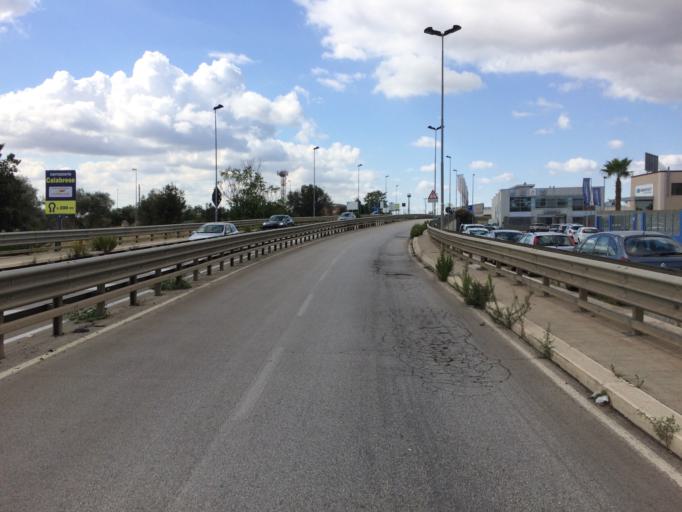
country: IT
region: Apulia
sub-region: Provincia di Bari
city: Bari
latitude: 41.1012
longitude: 16.8345
